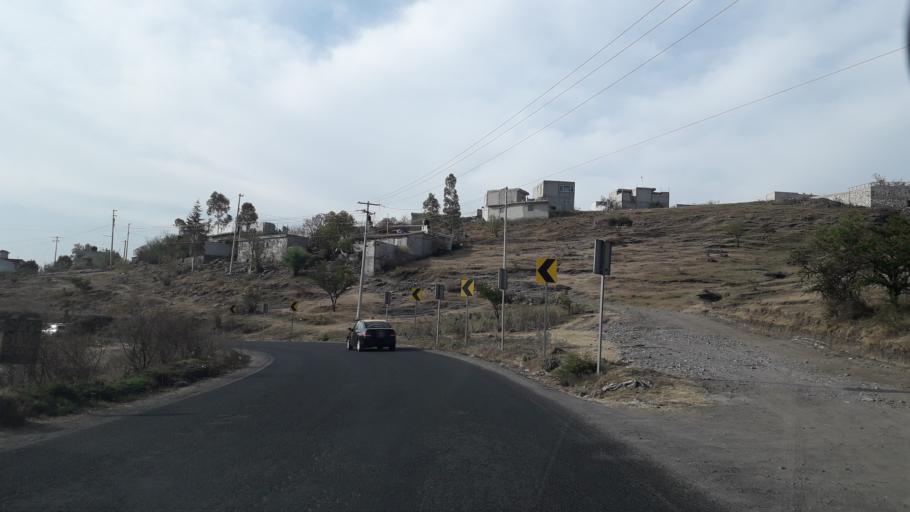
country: MX
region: Puebla
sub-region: Puebla
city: San Andres Azumiatla
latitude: 18.9236
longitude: -98.2528
